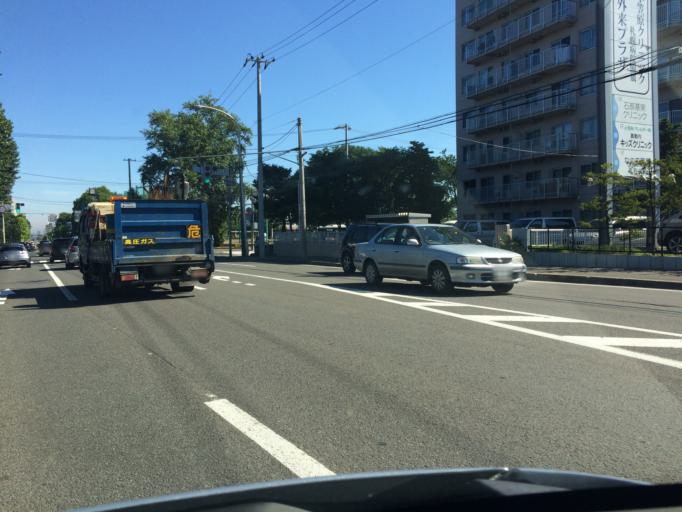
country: JP
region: Hokkaido
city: Sapporo
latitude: 42.9975
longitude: 141.3490
